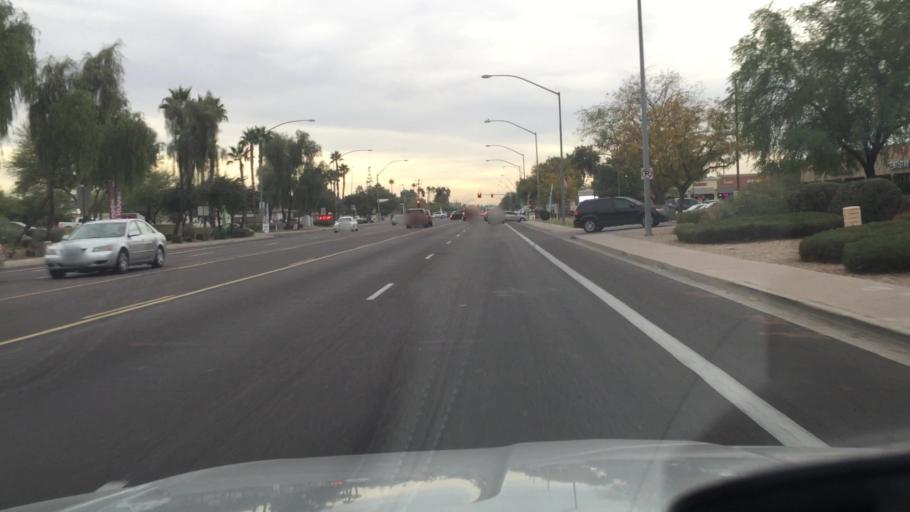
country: US
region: Arizona
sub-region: Maricopa County
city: Gilbert
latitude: 33.3958
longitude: -111.7539
